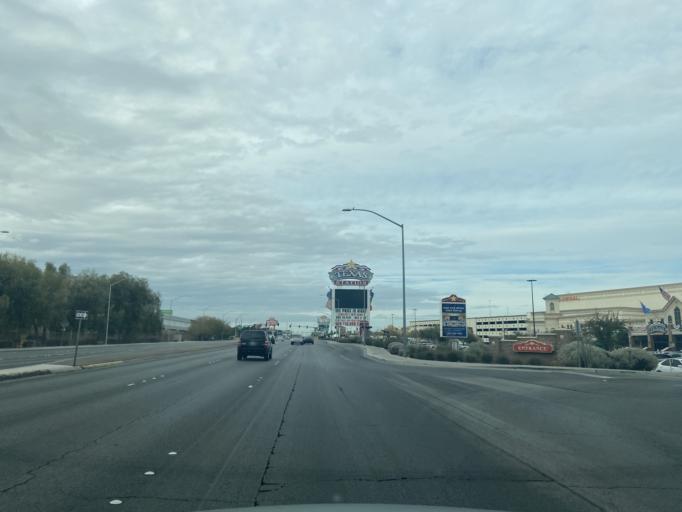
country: US
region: Nevada
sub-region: Clark County
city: Las Vegas
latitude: 36.1962
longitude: -115.1928
